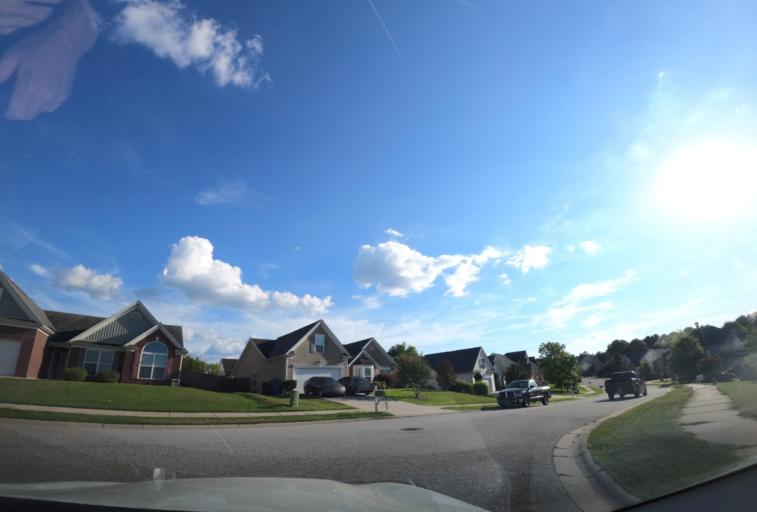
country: US
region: Georgia
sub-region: Columbia County
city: Grovetown
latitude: 33.5098
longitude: -82.2337
